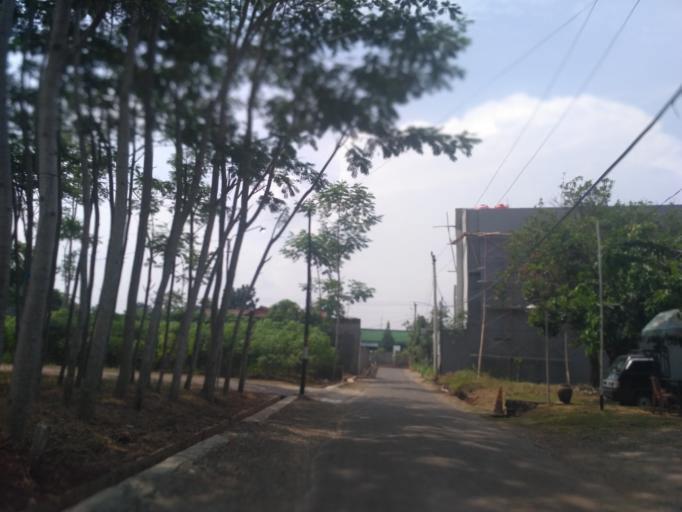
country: ID
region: Central Java
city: Ungaran
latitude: -7.0722
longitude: 110.4408
